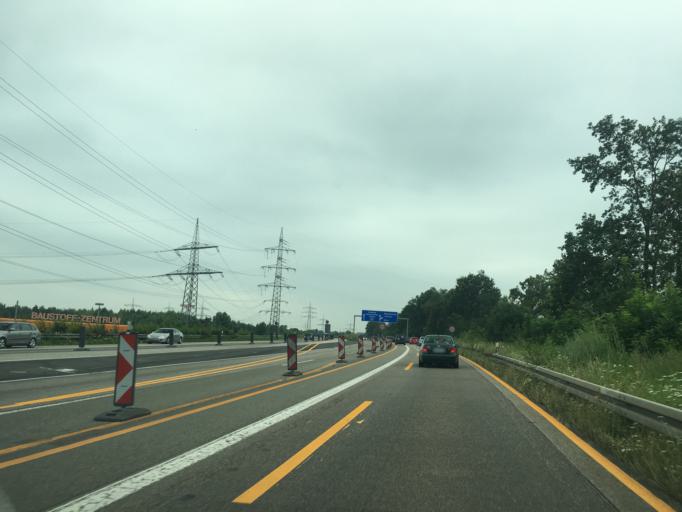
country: DE
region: North Rhine-Westphalia
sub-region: Regierungsbezirk Munster
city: Gelsenkirchen
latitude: 51.5288
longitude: 7.0757
